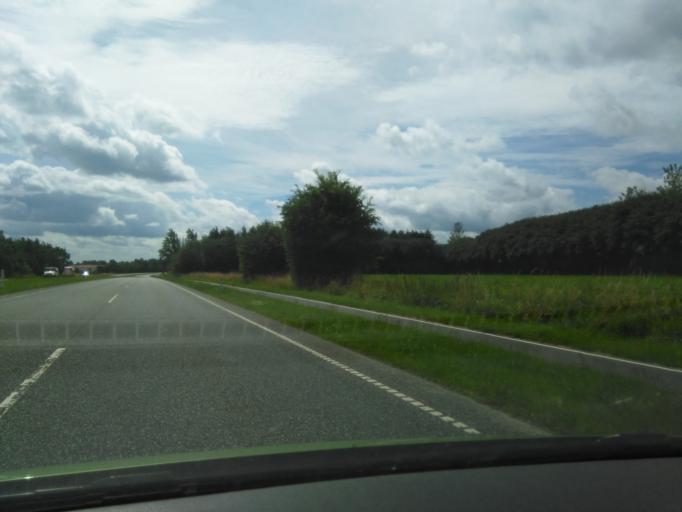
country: DK
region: Central Jutland
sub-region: Arhus Kommune
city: Hjortshoj
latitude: 56.2375
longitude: 10.2978
